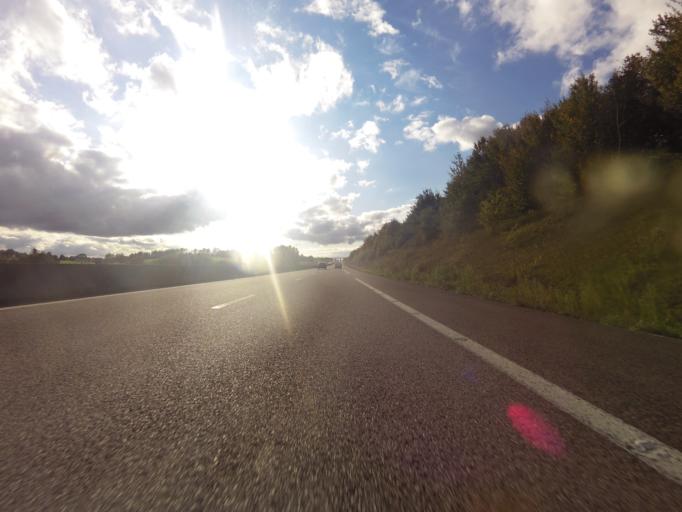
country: FR
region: Haute-Normandie
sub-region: Departement de la Seine-Maritime
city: Gaillefontaine
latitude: 49.7443
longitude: 1.6587
